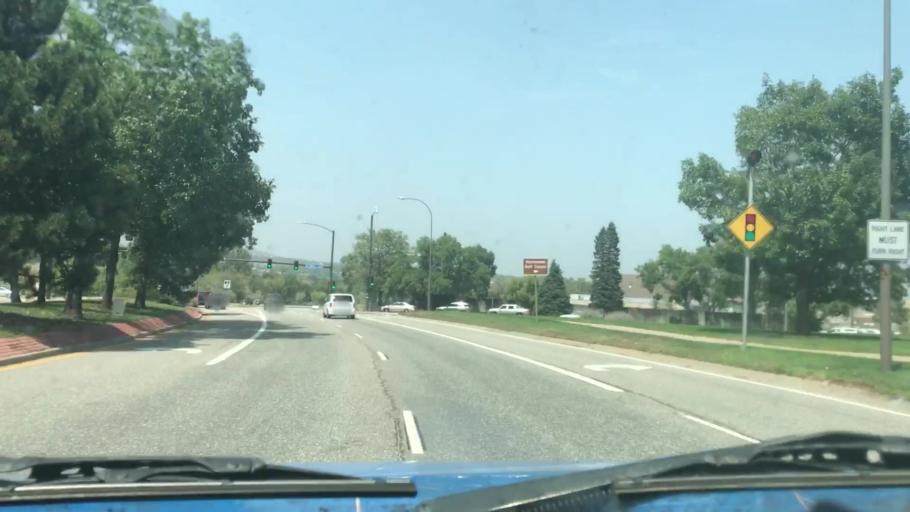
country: US
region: Colorado
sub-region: Jefferson County
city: Lakewood
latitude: 39.6554
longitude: -105.1100
